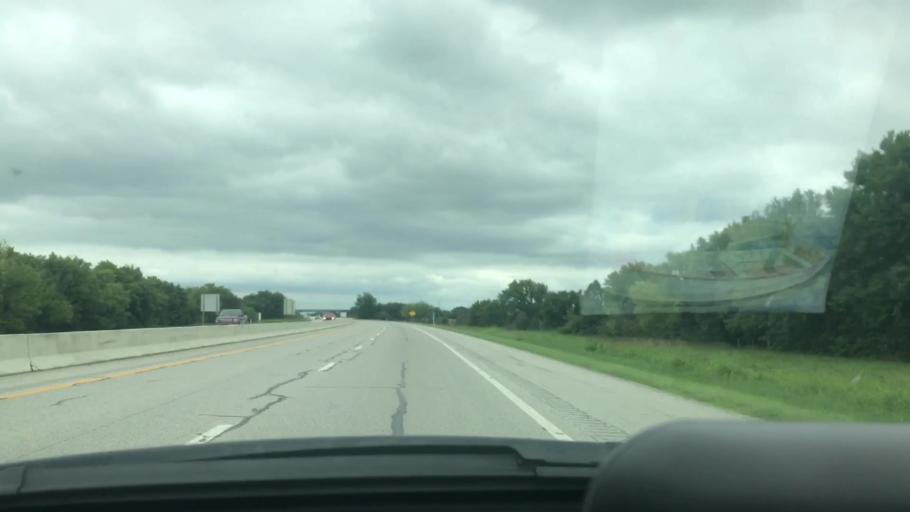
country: US
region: Oklahoma
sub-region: Ottawa County
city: Afton
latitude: 36.7368
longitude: -94.9132
